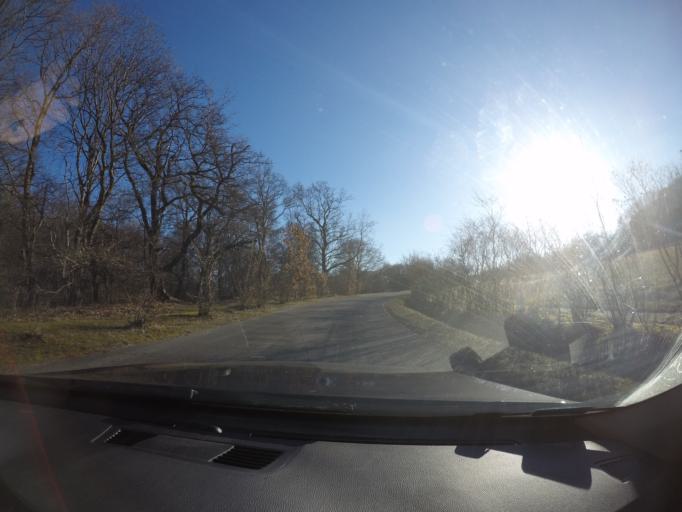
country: HU
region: Pest
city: Visegrad
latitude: 47.7979
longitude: 18.9961
